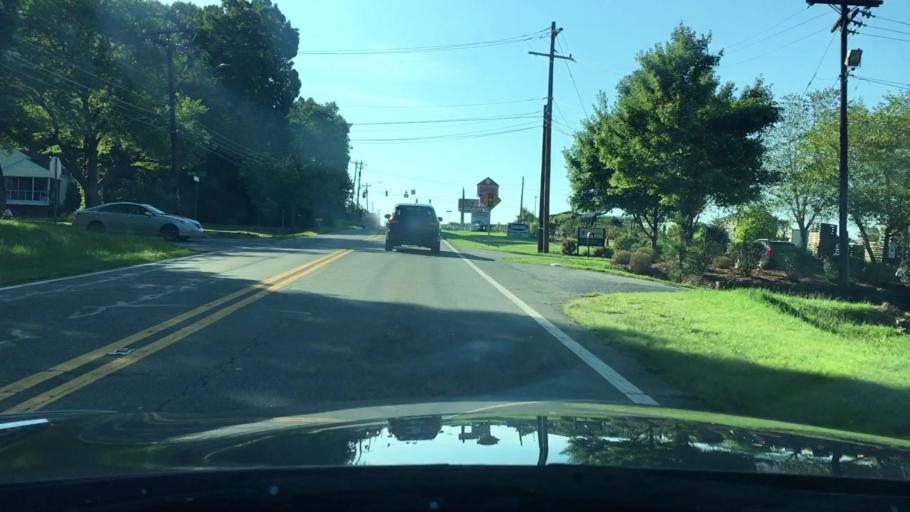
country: US
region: North Carolina
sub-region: Alamance County
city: Burlington
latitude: 36.0704
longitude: -79.4351
